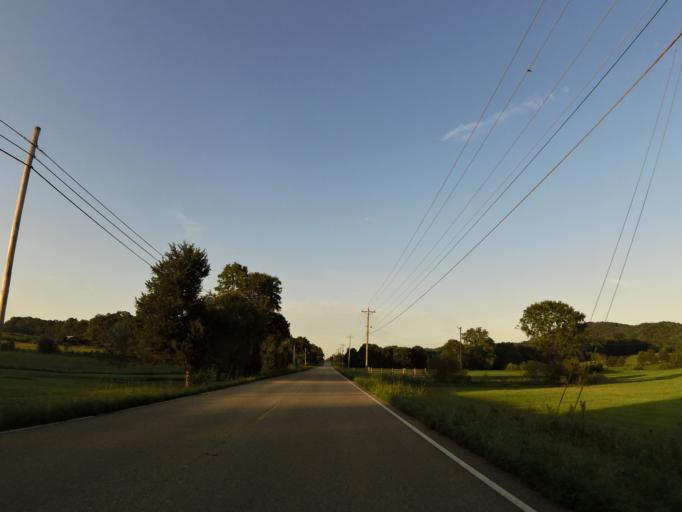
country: US
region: Tennessee
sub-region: Roane County
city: Midtown
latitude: 35.7587
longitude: -84.6014
